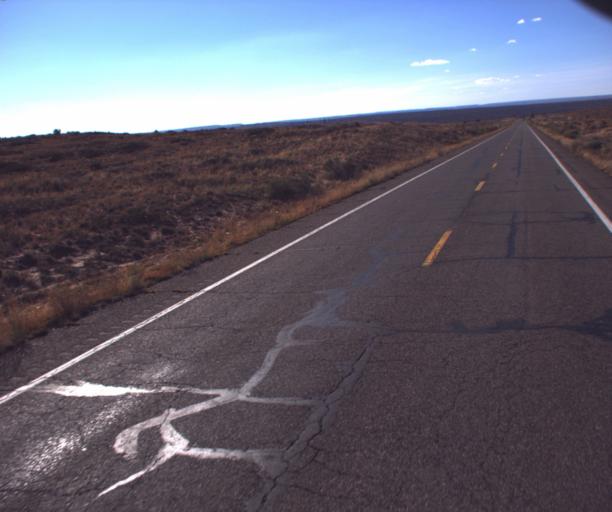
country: US
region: Arizona
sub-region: Coconino County
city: Kaibito
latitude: 36.6126
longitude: -111.0397
